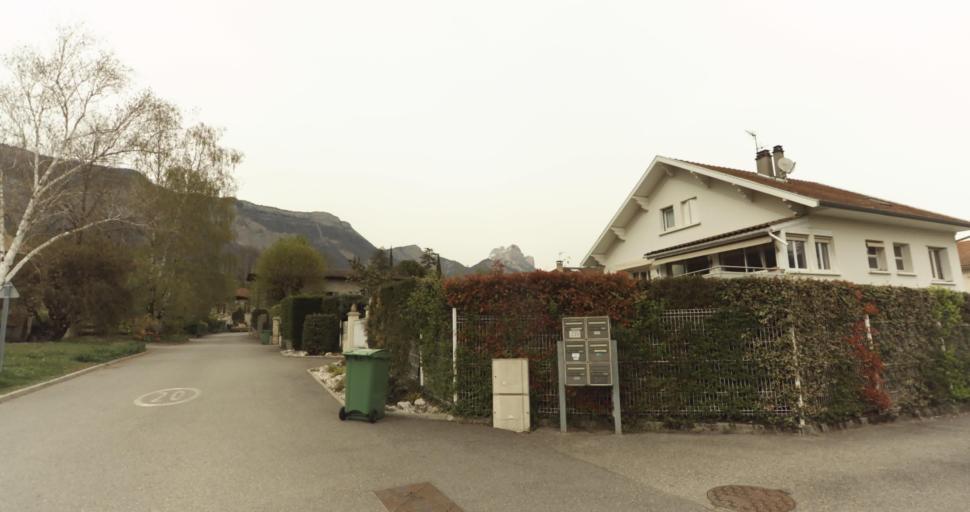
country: FR
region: Rhone-Alpes
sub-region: Departement de l'Isere
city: Montbonnot-Saint-Martin
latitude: 45.2288
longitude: 5.8200
